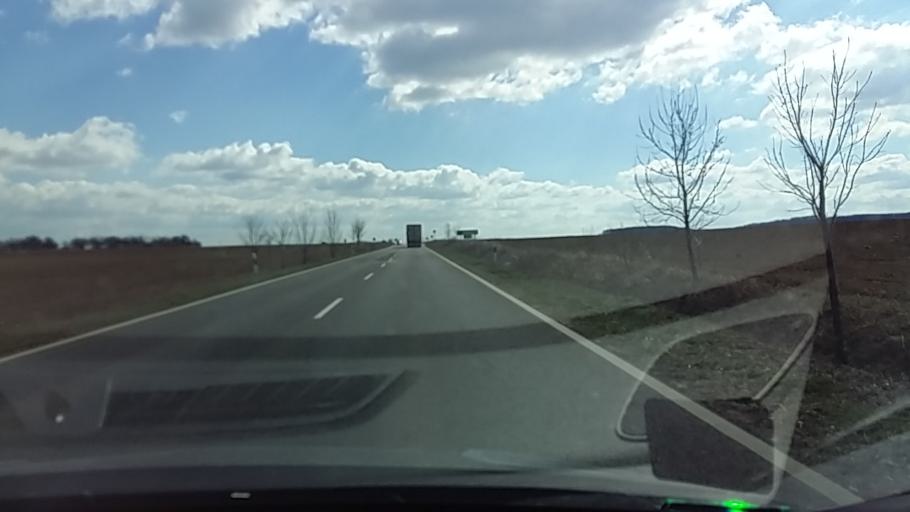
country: HU
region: Baranya
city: Kozarmisleny
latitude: 46.0395
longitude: 18.2723
